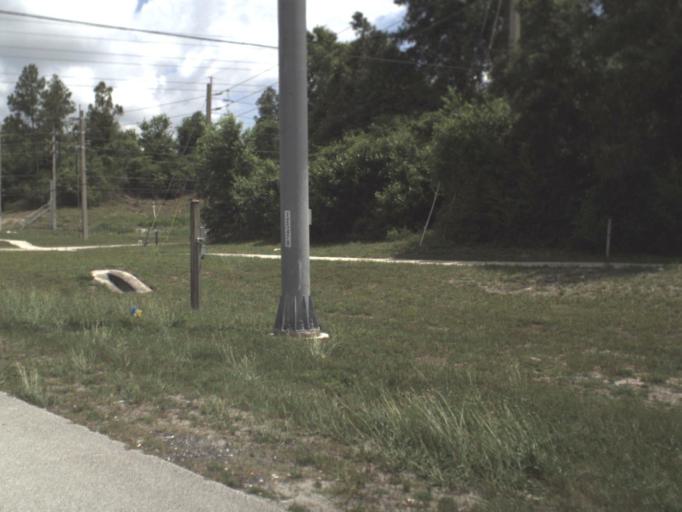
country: US
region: Florida
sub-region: Duval County
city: Jacksonville
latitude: 30.2351
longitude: -81.5519
